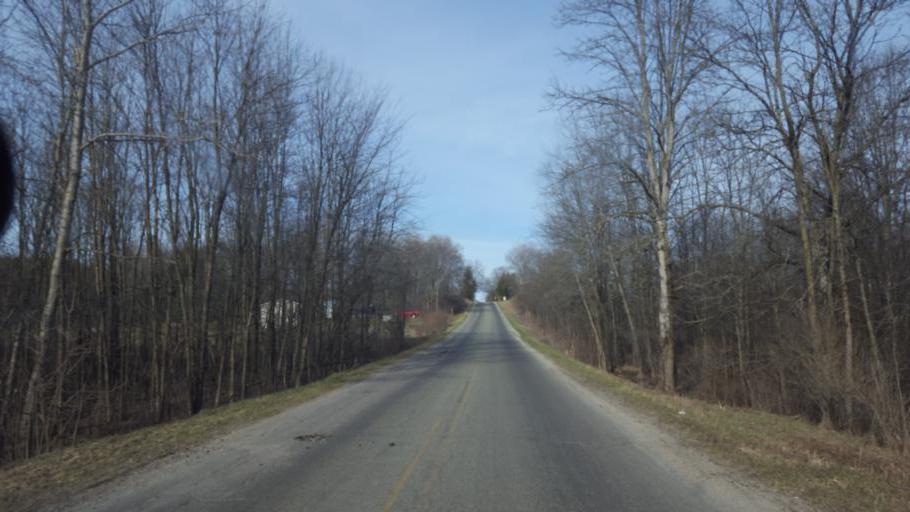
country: US
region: Michigan
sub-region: Montcalm County
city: Howard City
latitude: 43.5262
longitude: -85.4511
